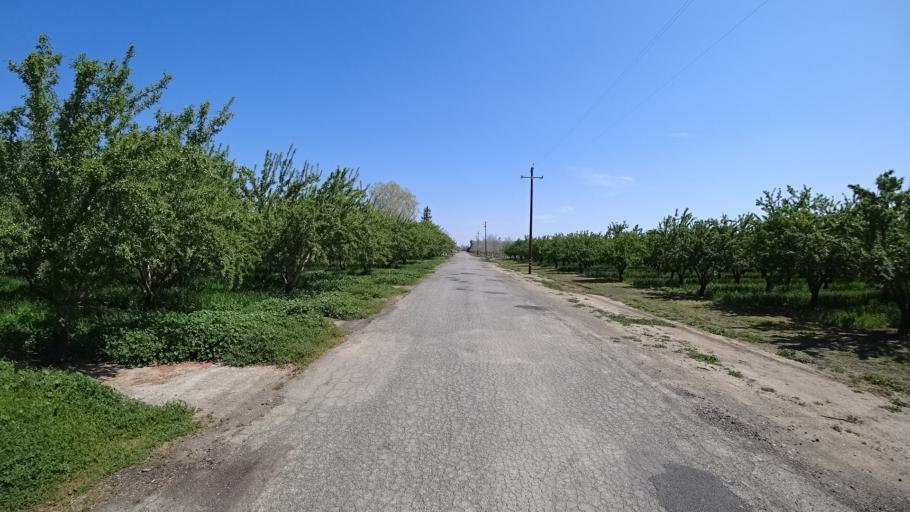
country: US
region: California
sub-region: Glenn County
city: Willows
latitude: 39.5364
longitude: -122.0271
